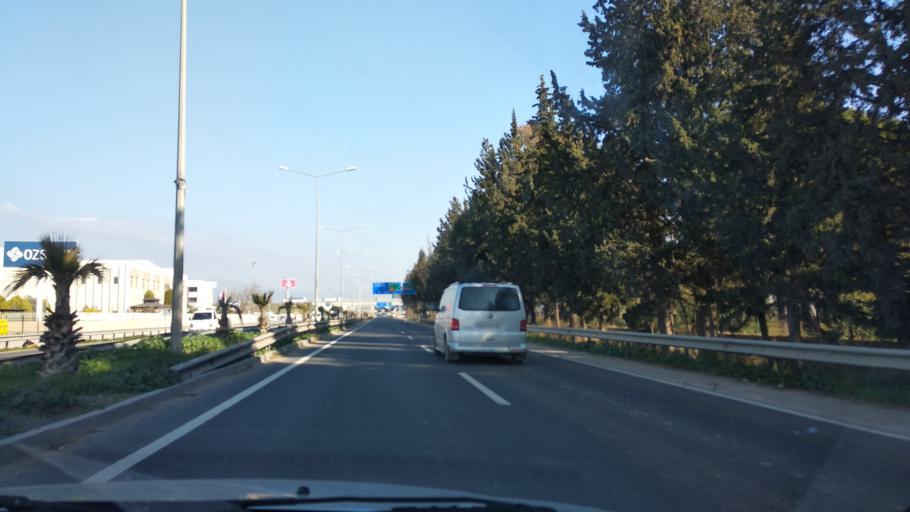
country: TR
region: Izmir
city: Menemen
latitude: 38.5674
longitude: 27.0529
